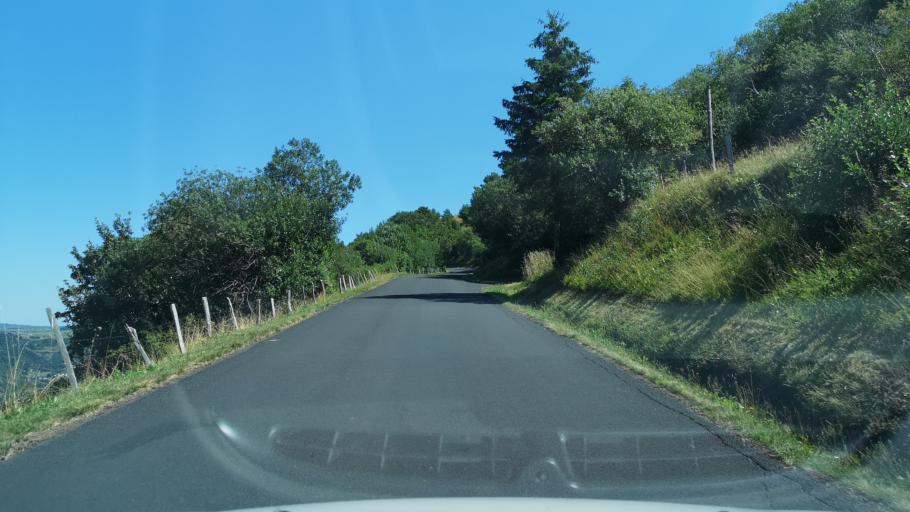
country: FR
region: Auvergne
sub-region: Departement du Puy-de-Dome
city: Mont-Dore
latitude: 45.5486
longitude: 2.8814
